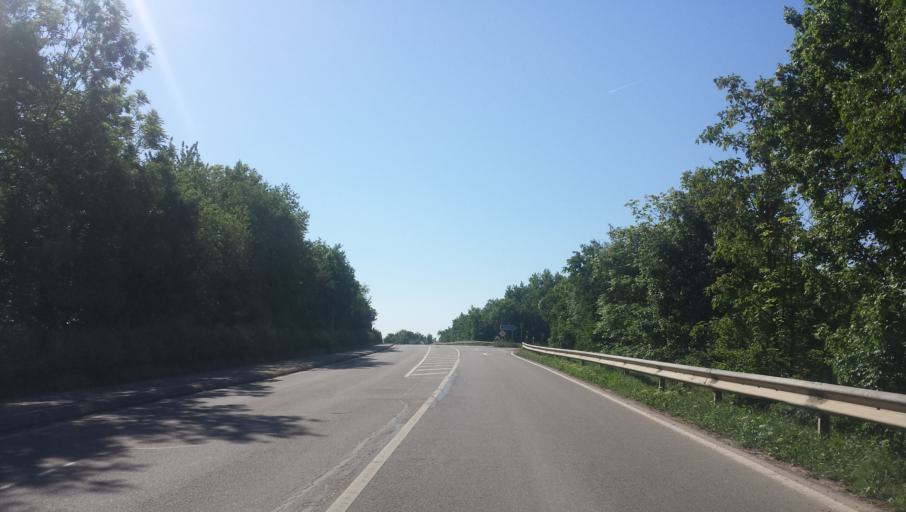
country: DE
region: Rheinland-Pfalz
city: Mutterstadt
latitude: 49.4523
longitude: 8.3430
